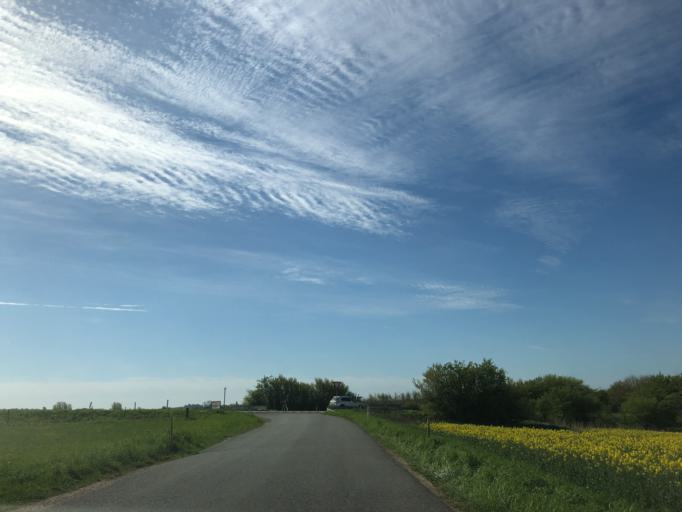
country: DK
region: Zealand
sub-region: Slagelse Kommune
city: Forlev
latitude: 55.3784
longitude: 11.2979
